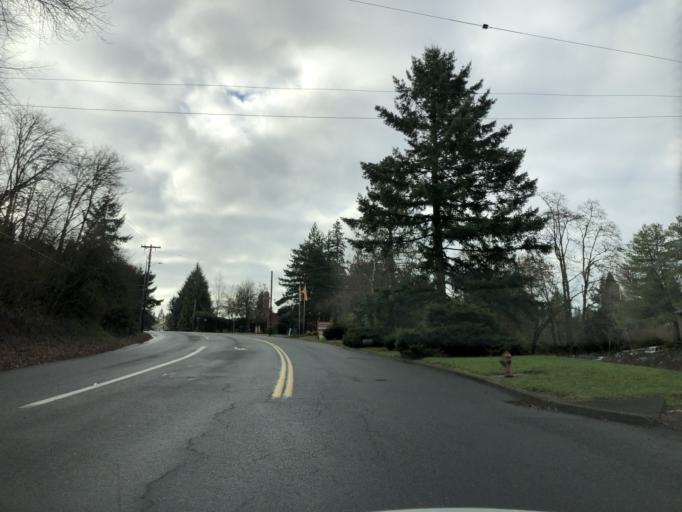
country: US
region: Oregon
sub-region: Washington County
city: Metzger
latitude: 45.4545
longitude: -122.7124
